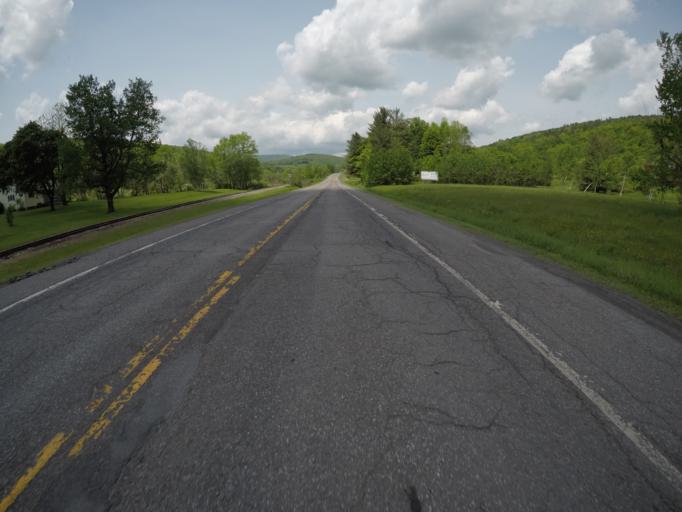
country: US
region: New York
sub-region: Delaware County
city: Stamford
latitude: 42.1989
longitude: -74.5980
